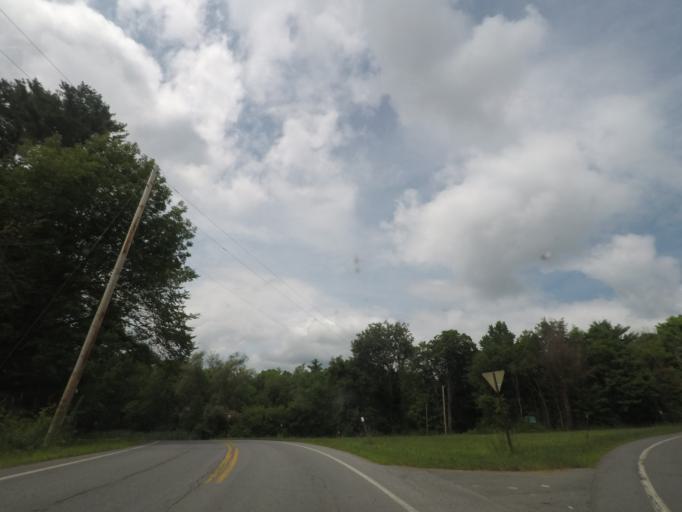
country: US
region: New York
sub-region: Saratoga County
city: Schuylerville
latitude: 43.0487
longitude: -73.6774
